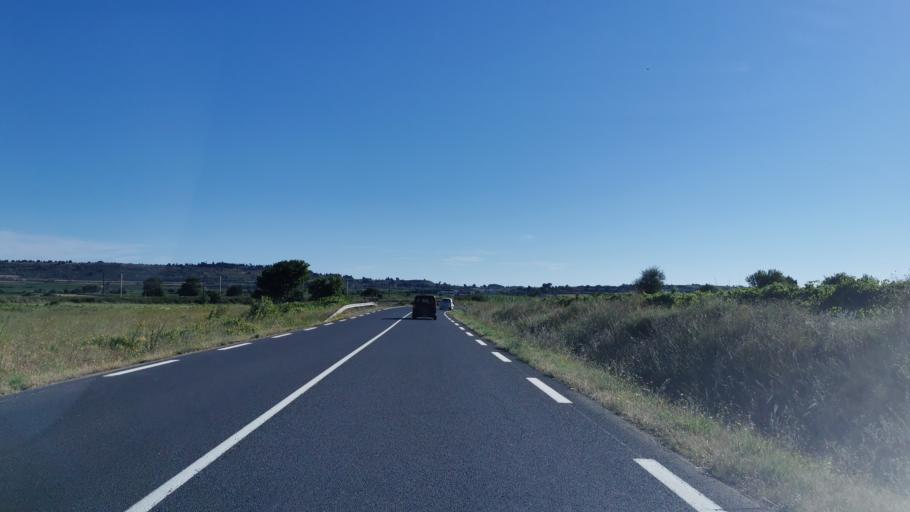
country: FR
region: Languedoc-Roussillon
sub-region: Departement de l'Herault
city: Nissan-lez-Enserune
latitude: 43.2835
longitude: 3.1042
